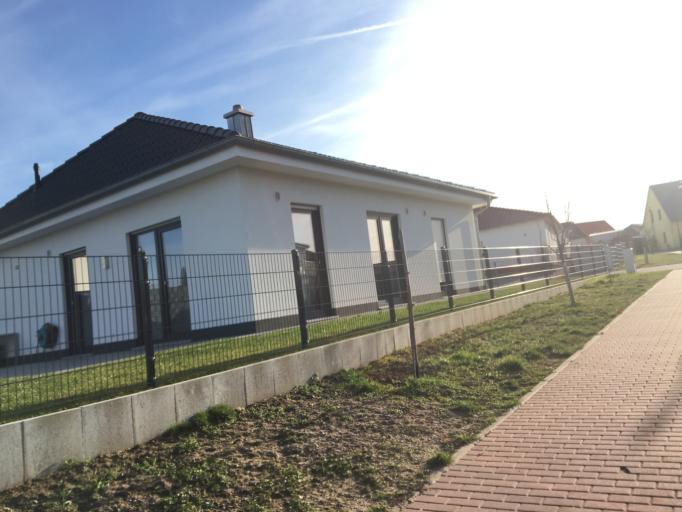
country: DE
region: Bavaria
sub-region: Regierungsbezirk Mittelfranken
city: Wilhermsdorf
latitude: 49.4756
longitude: 10.7241
